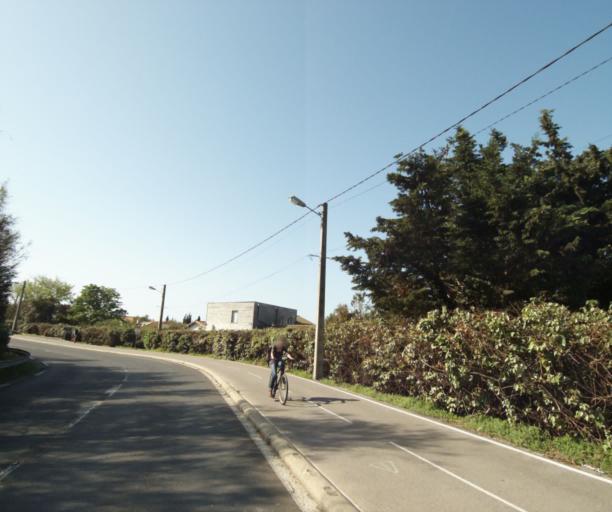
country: FR
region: Languedoc-Roussillon
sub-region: Departement de l'Herault
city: Perols
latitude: 43.5545
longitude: 3.9667
